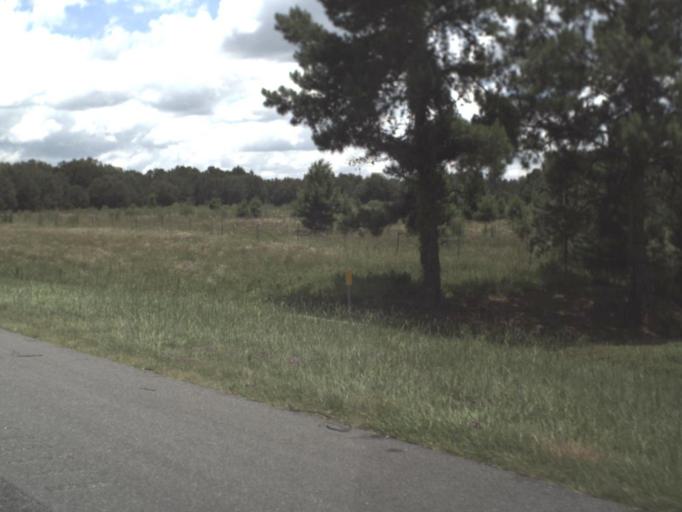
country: US
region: Florida
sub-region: Alachua County
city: High Springs
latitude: 29.9969
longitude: -82.5910
